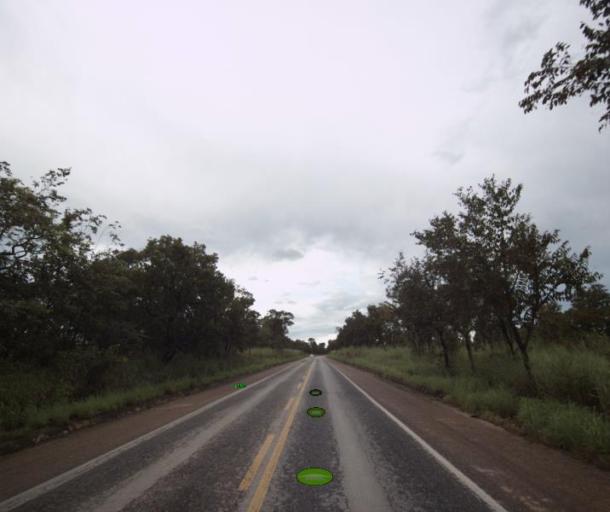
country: BR
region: Goias
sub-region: Porangatu
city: Porangatu
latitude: -13.6767
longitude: -49.0253
